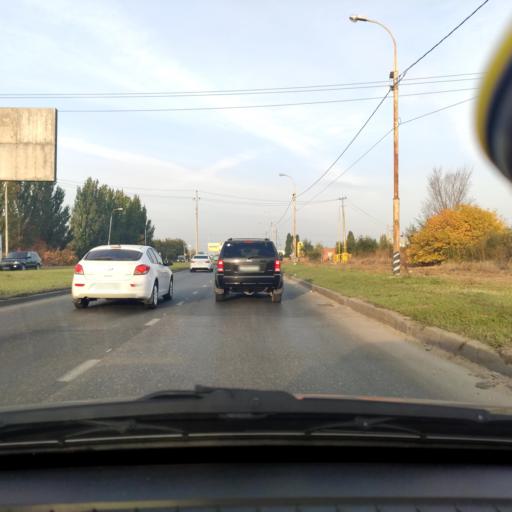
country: RU
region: Samara
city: Tol'yatti
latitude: 53.5608
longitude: 49.2947
